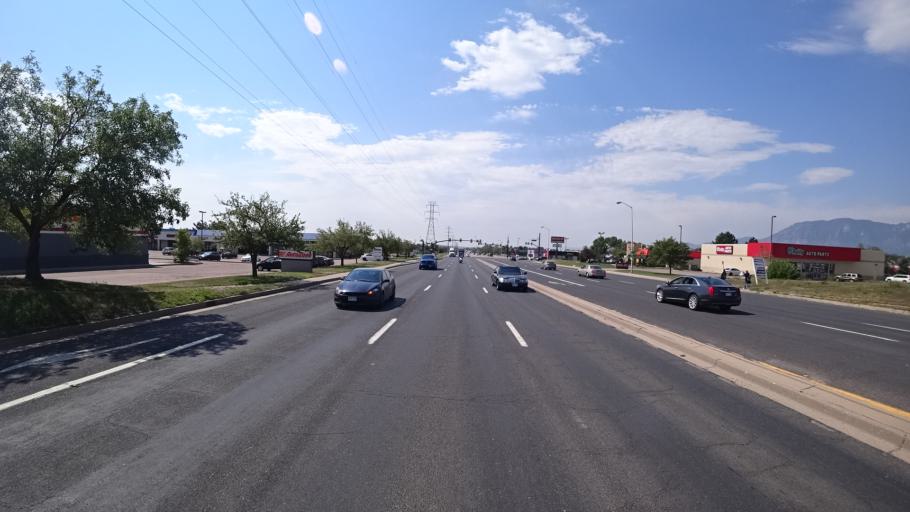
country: US
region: Colorado
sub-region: El Paso County
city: Stratmoor
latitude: 38.8062
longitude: -104.7575
